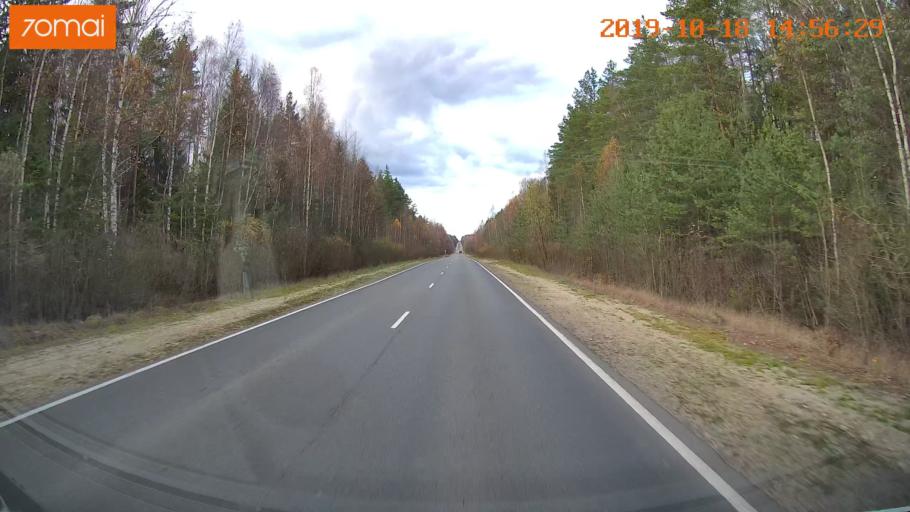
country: RU
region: Vladimir
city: Kurlovo
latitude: 55.4654
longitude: 40.5871
